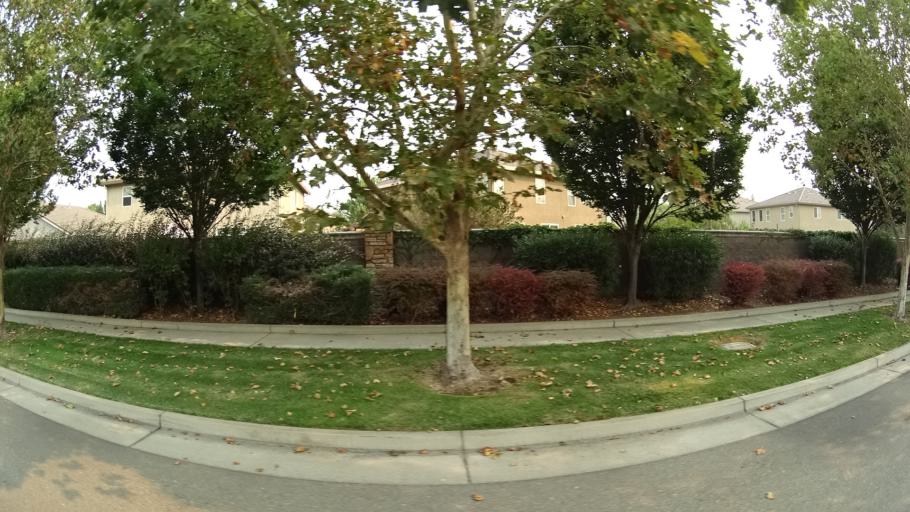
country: US
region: California
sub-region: Sacramento County
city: Laguna
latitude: 38.3974
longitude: -121.4487
